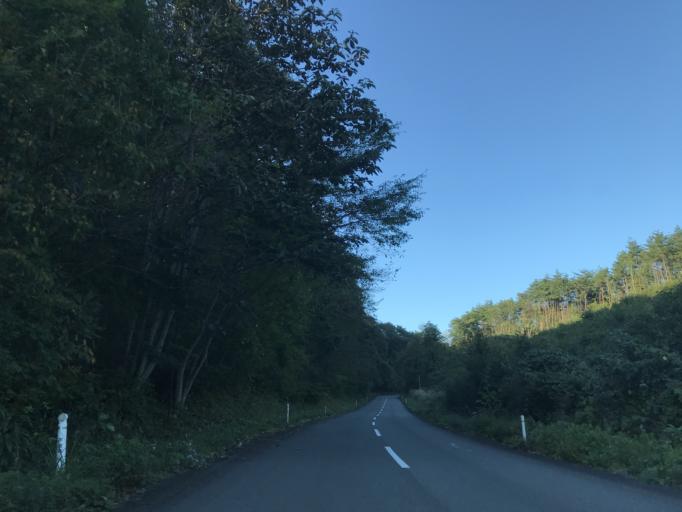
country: JP
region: Iwate
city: Ichinoseki
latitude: 38.9979
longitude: 141.0439
